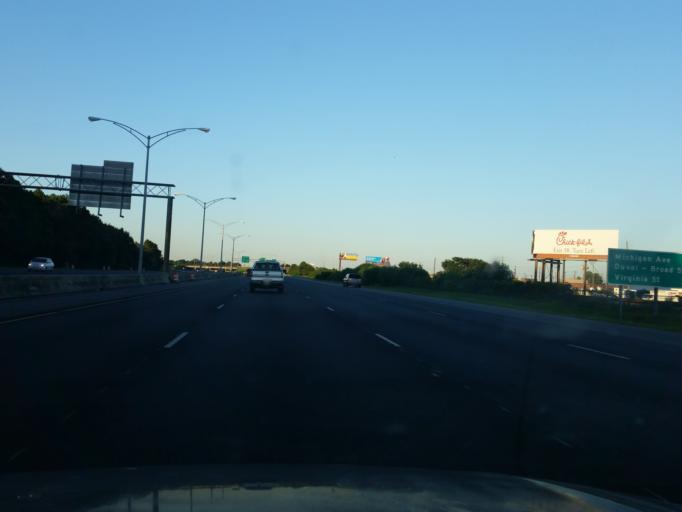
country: US
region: Alabama
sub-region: Mobile County
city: Mobile
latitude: 30.6440
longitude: -88.0821
